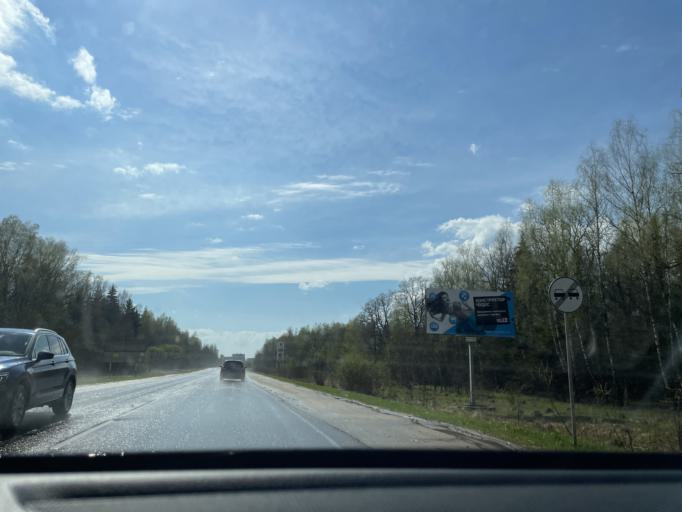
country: RU
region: Tula
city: Aleksin
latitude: 54.5137
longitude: 37.1362
